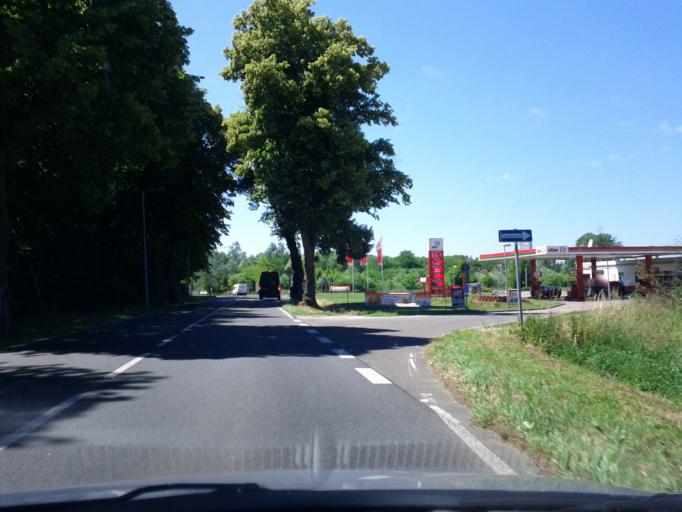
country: DE
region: Brandenburg
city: Rehfelde
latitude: 52.4815
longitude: 13.8640
